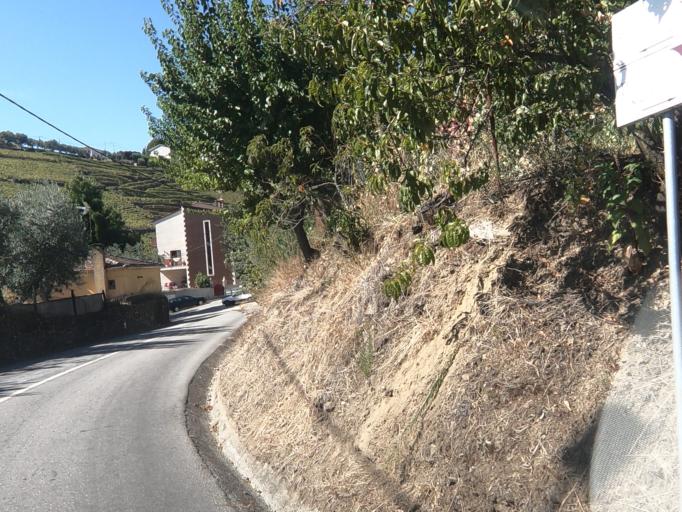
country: PT
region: Vila Real
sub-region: Santa Marta de Penaguiao
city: Santa Marta de Penaguiao
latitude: 41.2180
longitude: -7.7859
